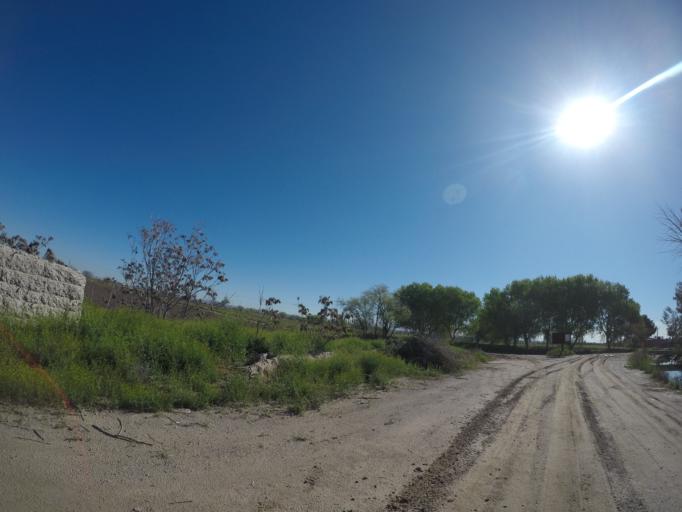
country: US
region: Texas
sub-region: El Paso County
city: Socorro
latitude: 31.6466
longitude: -106.3396
